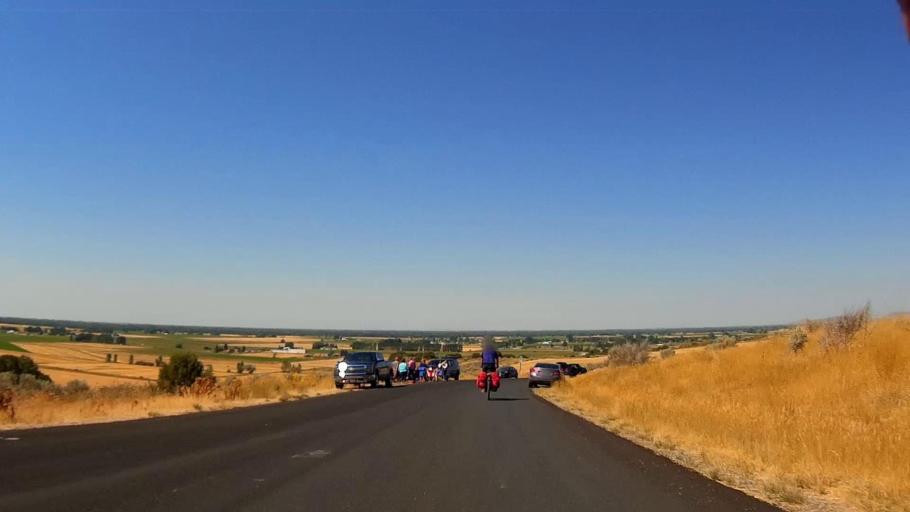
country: US
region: Idaho
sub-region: Madison County
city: Rexburg
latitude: 43.7176
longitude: -111.7475
